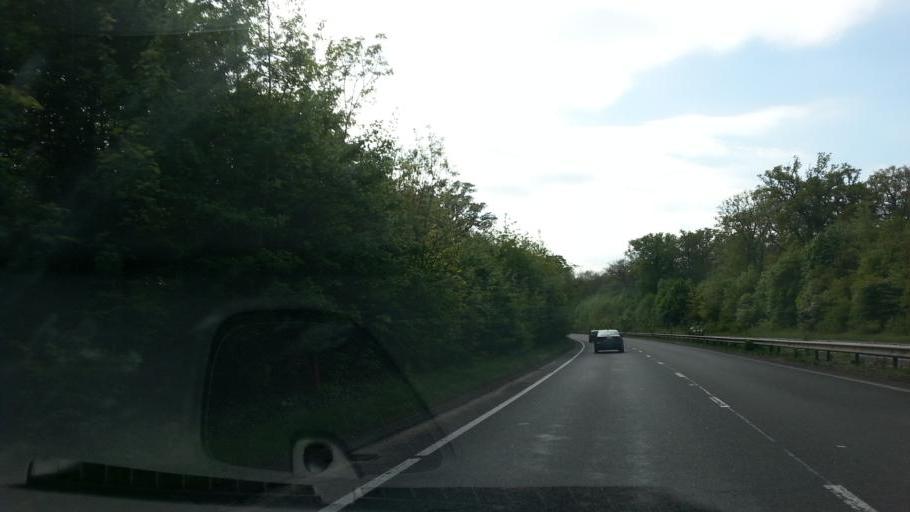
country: GB
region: England
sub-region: Peterborough
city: Marholm
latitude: 52.5725
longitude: -0.3067
